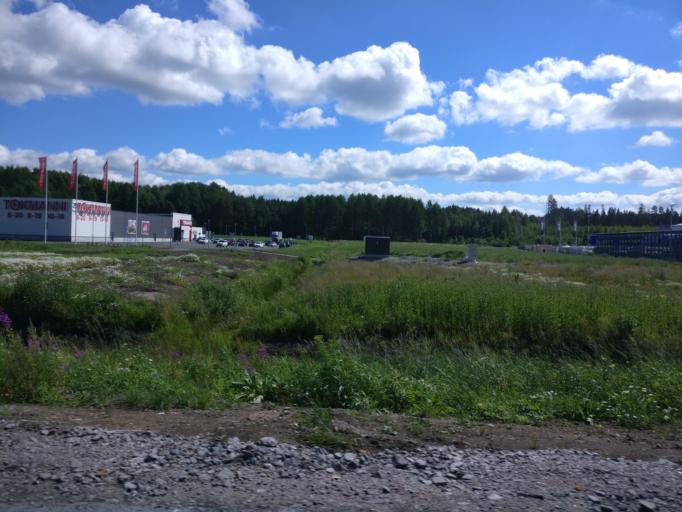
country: FI
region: Southern Savonia
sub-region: Savonlinna
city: Savonlinna
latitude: 61.8740
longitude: 28.9520
